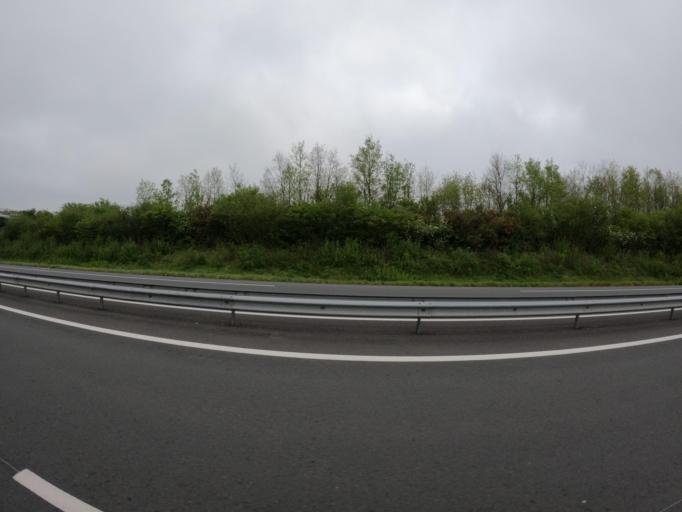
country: FR
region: Pays de la Loire
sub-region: Departement de la Vendee
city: Vendrennes
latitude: 46.8658
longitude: -1.1330
